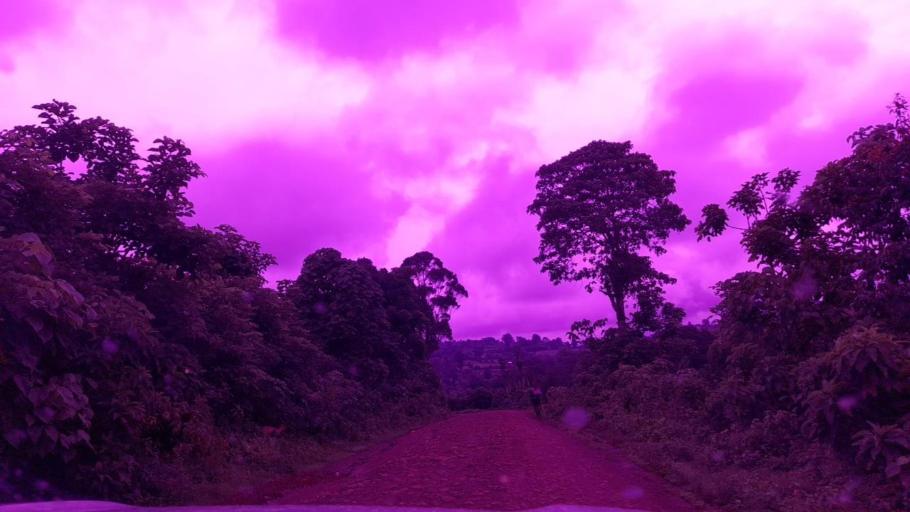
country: ET
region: Southern Nations, Nationalities, and People's Region
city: Tippi
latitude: 7.5833
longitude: 35.7720
